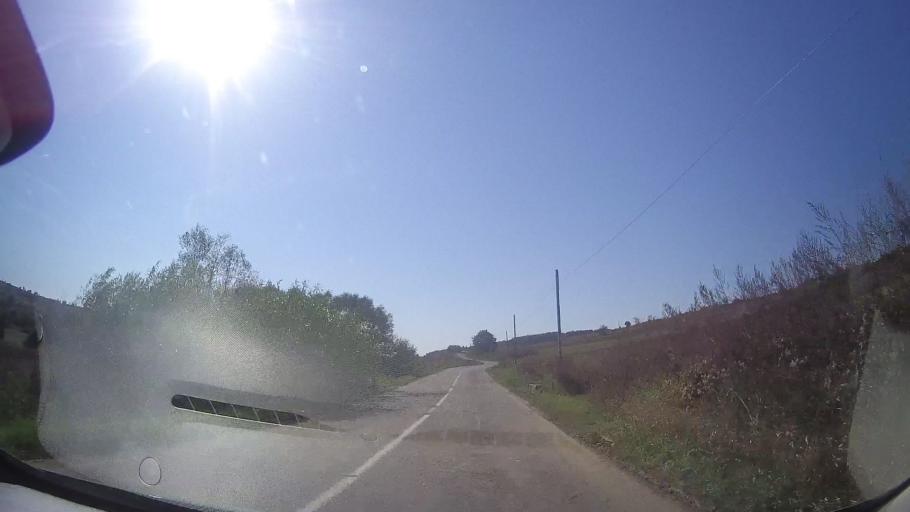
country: RO
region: Timis
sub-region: Comuna Ohaba Lunga
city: Ohaba Lunga
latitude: 45.8976
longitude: 21.9739
